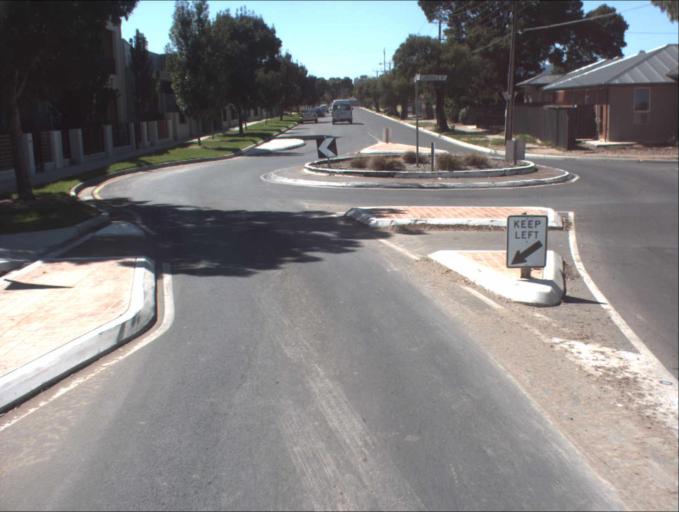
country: AU
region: South Australia
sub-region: Port Adelaide Enfield
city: Klemzig
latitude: -34.8652
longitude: 138.6333
